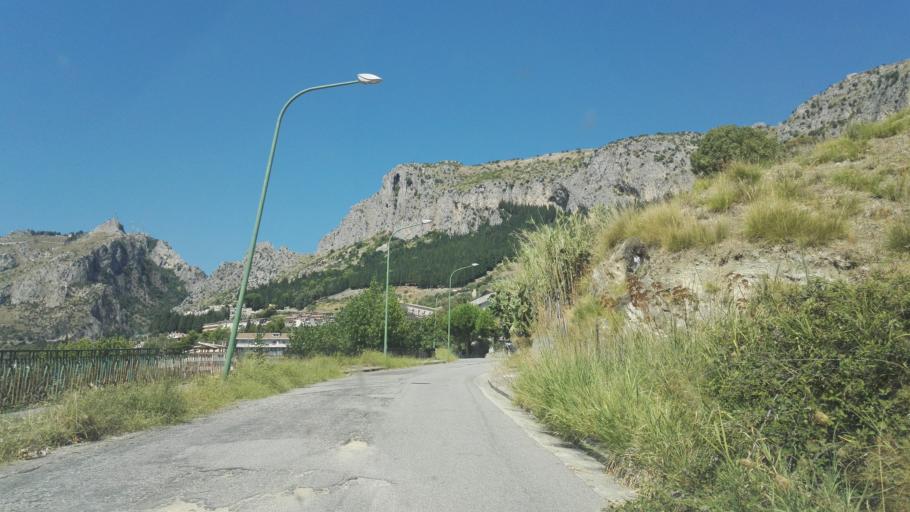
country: IT
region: Calabria
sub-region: Provincia di Reggio Calabria
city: Stilo
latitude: 38.4749
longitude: 16.4707
